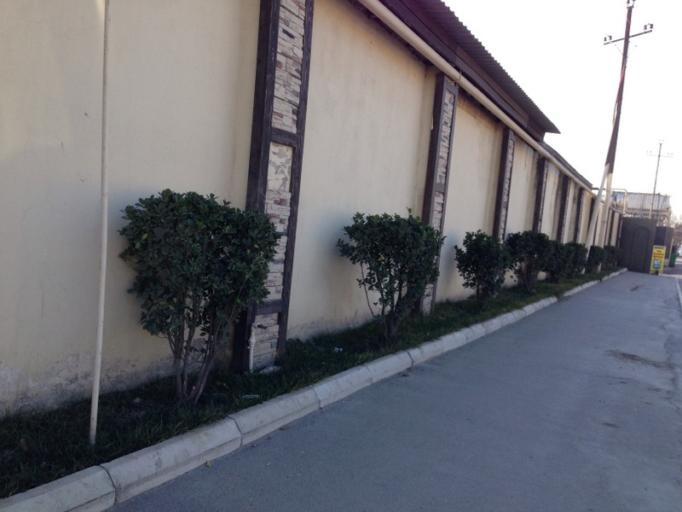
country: AZ
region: Baki
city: Binagadi
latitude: 40.4202
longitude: 49.8570
